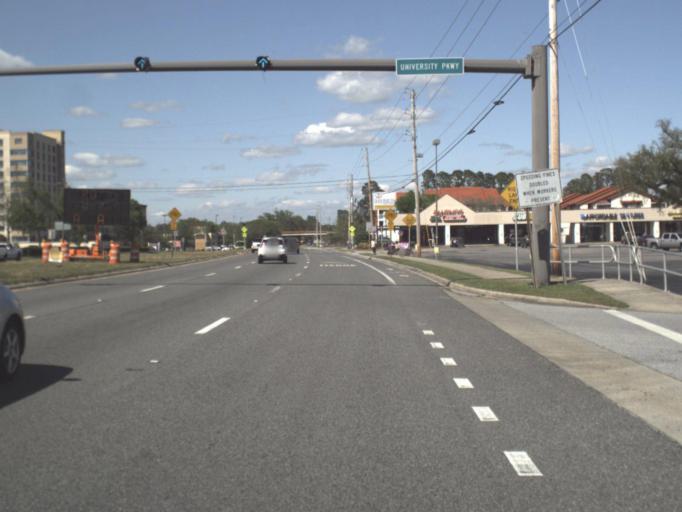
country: US
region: Florida
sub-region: Escambia County
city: Ferry Pass
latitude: 30.5115
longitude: -87.2196
